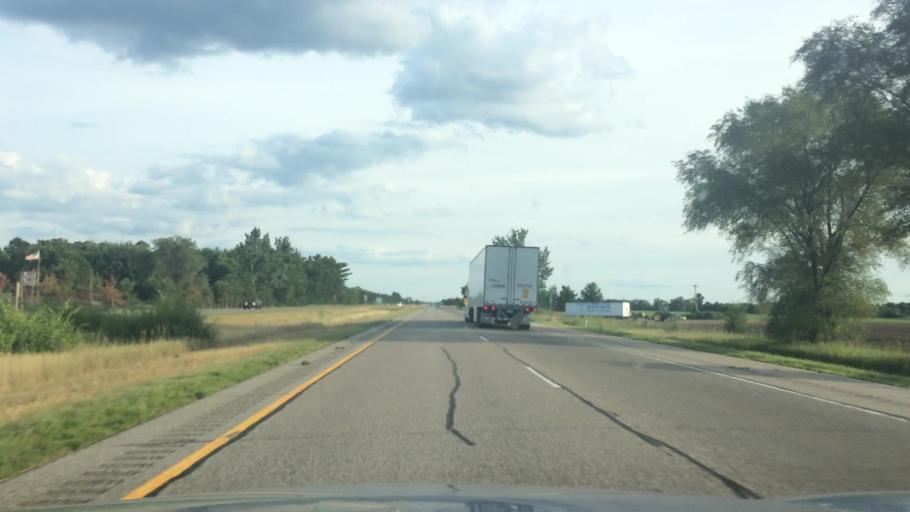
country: US
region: Wisconsin
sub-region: Portage County
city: Plover
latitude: 44.2466
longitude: -89.5243
